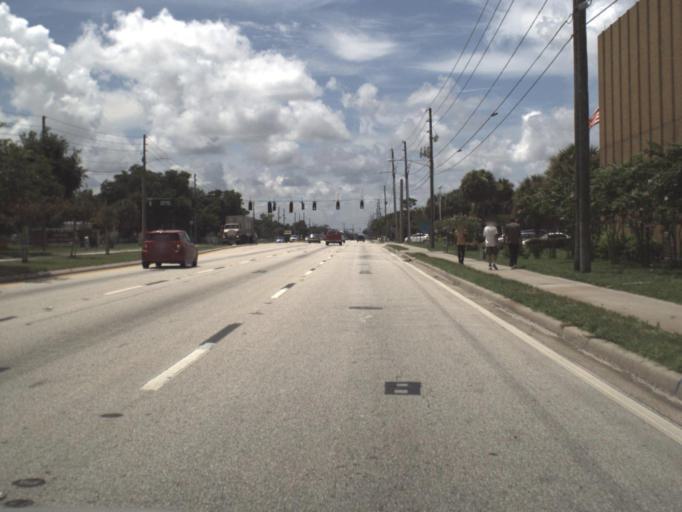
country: US
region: Florida
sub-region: Pinellas County
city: South Highpoint
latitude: 27.9041
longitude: -82.7007
